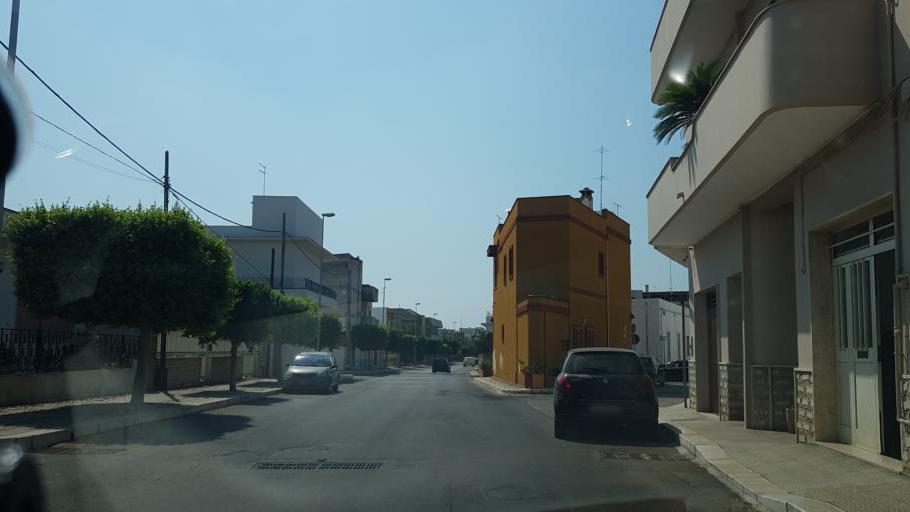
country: IT
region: Apulia
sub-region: Provincia di Taranto
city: Maruggio
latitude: 40.3255
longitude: 17.5733
